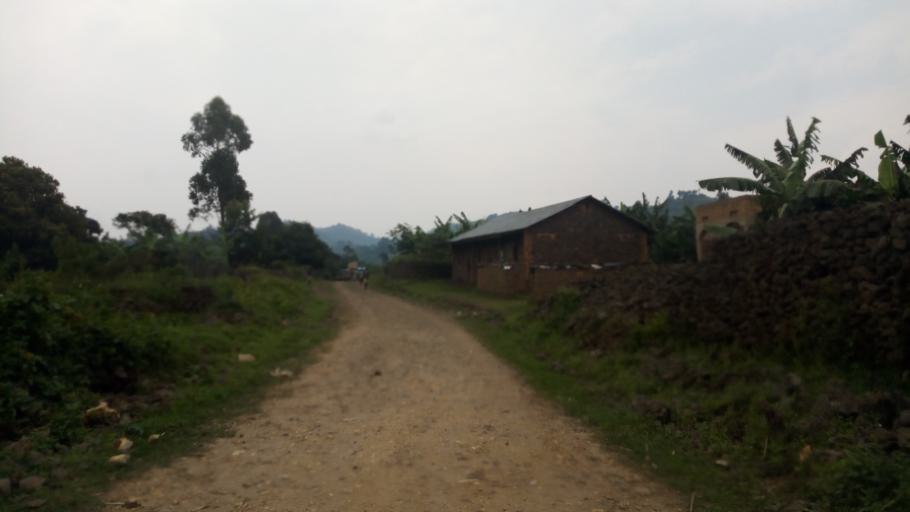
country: UG
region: Western Region
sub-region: Kisoro District
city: Kisoro
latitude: -1.2659
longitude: 29.6261
